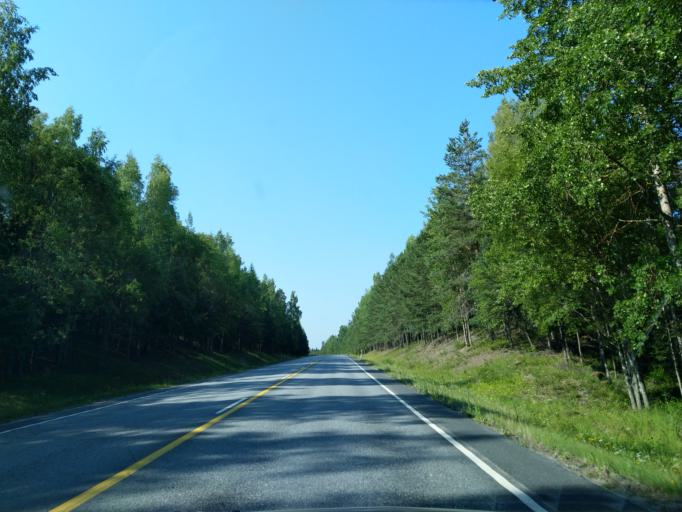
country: FI
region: Satakunta
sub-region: Pori
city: Noormarkku
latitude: 61.6192
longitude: 21.9042
